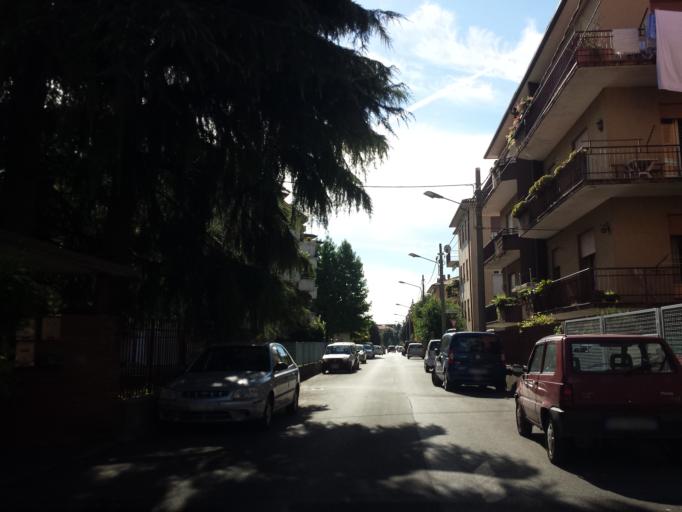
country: IT
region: Veneto
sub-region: Provincia di Vicenza
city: Vicenza
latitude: 45.5625
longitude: 11.5599
